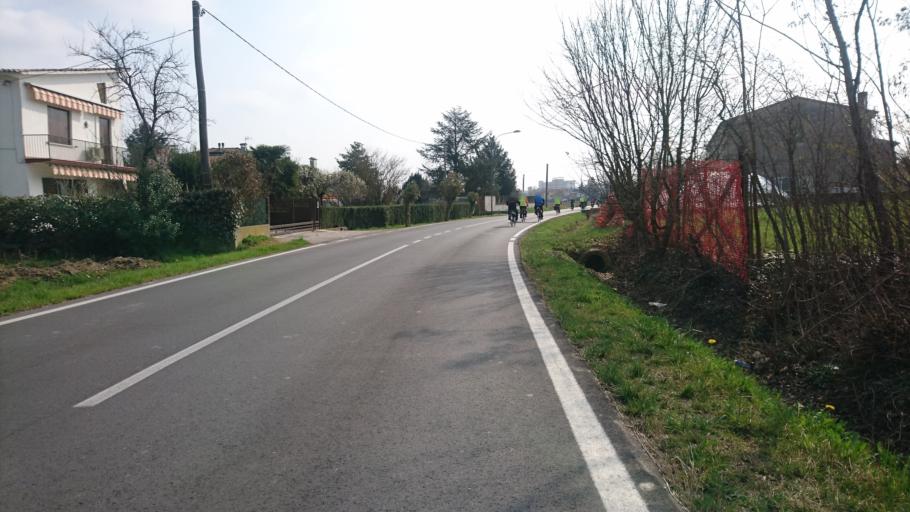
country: IT
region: Veneto
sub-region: Provincia di Padova
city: Abano Terme
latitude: 45.3603
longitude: 11.7678
